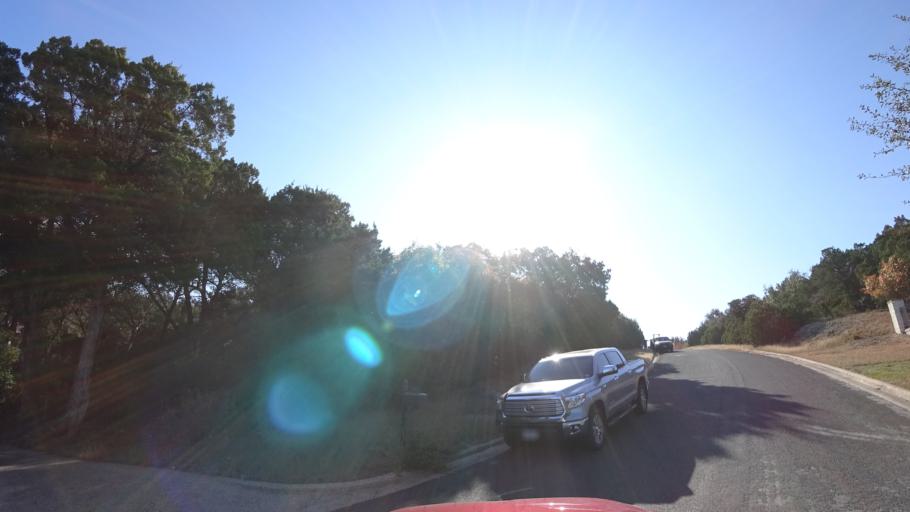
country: US
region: Texas
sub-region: Williamson County
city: Anderson Mill
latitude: 30.3783
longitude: -97.8237
